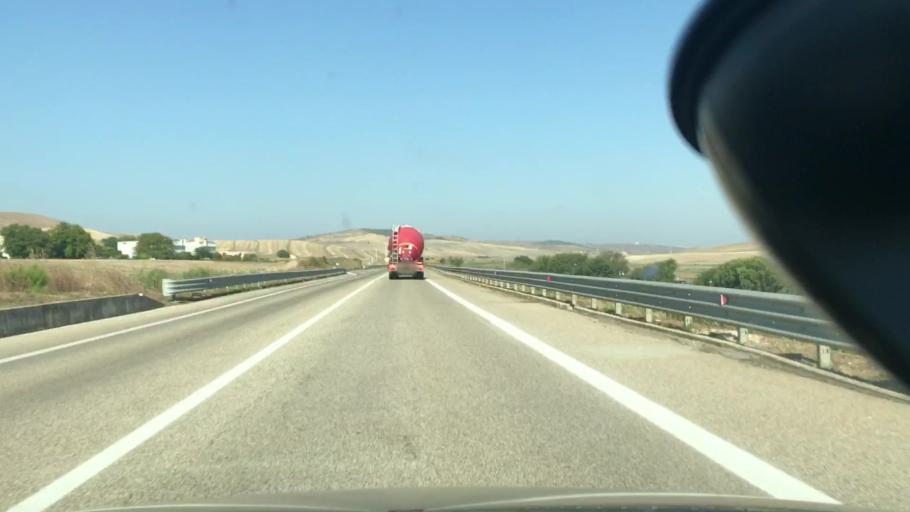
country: IT
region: Basilicate
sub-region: Provincia di Matera
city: Irsina
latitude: 40.7840
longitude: 16.3024
